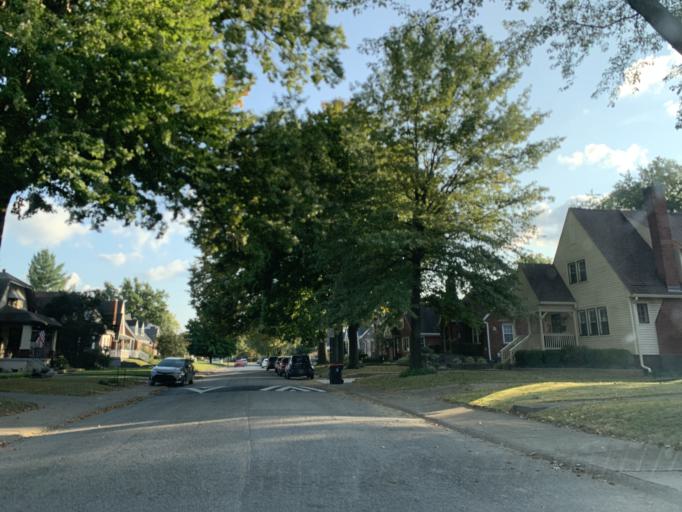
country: US
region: Kentucky
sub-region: Jefferson County
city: Audubon Park
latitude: 38.1890
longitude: -85.7627
